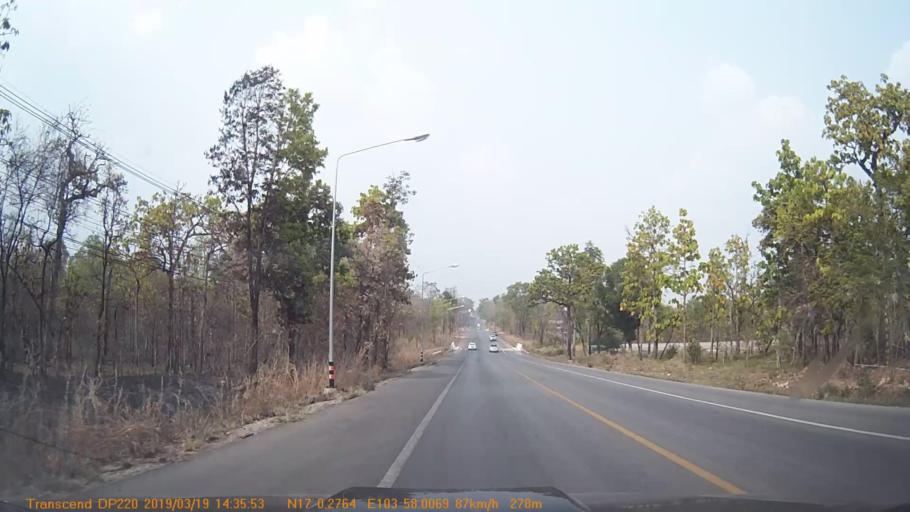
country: TH
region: Sakon Nakhon
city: Phu Phan
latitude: 17.0047
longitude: 103.9668
